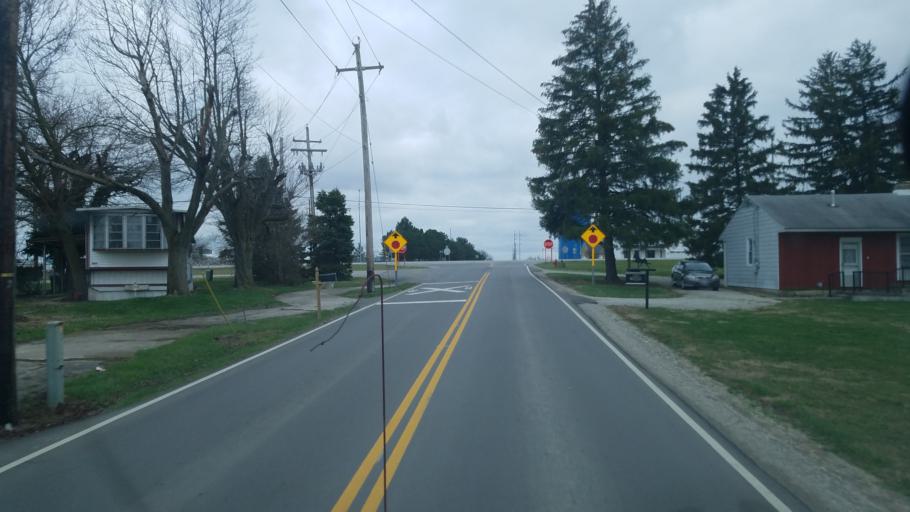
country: US
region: Ohio
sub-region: Fayette County
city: Washington Court House
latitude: 39.5282
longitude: -83.4711
